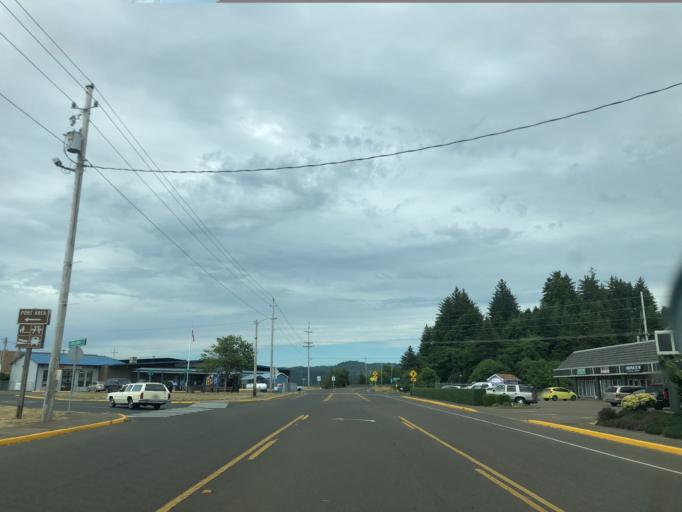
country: US
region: Oregon
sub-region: Lincoln County
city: Waldport
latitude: 44.4292
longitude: -124.0603
